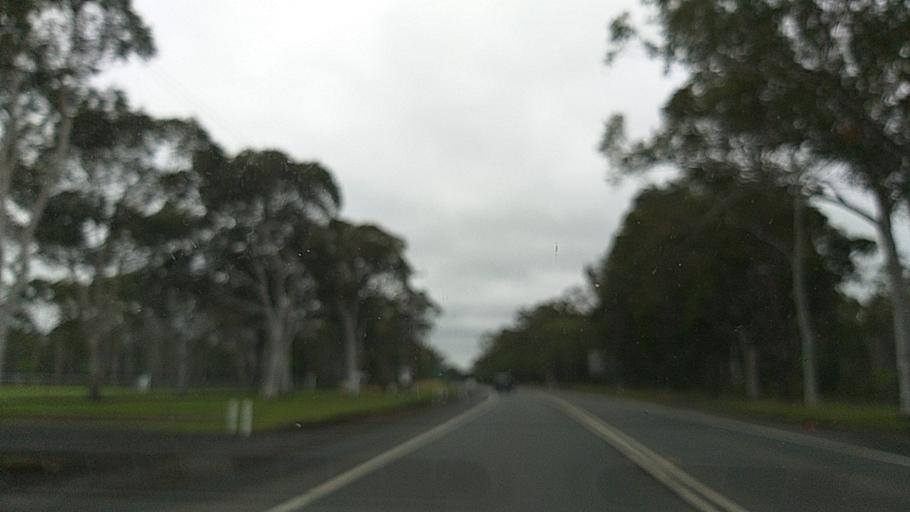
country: AU
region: New South Wales
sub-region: Penrith Municipality
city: Werrington Downs
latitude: -33.6888
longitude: 150.7304
